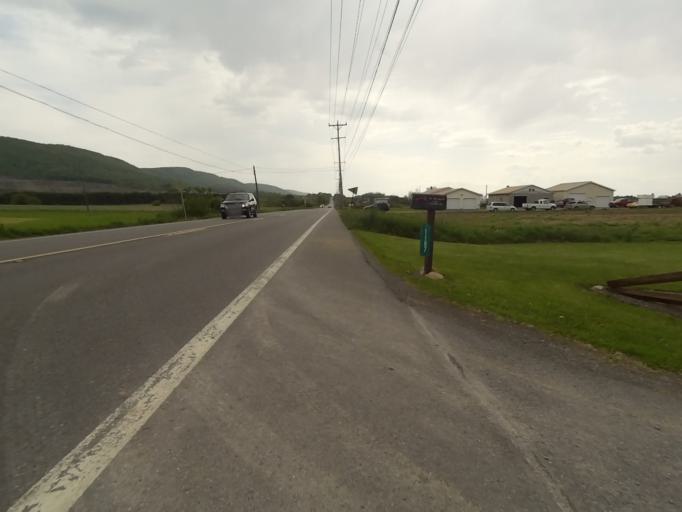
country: US
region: Pennsylvania
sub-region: Centre County
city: Zion
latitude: 40.8997
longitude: -77.6939
